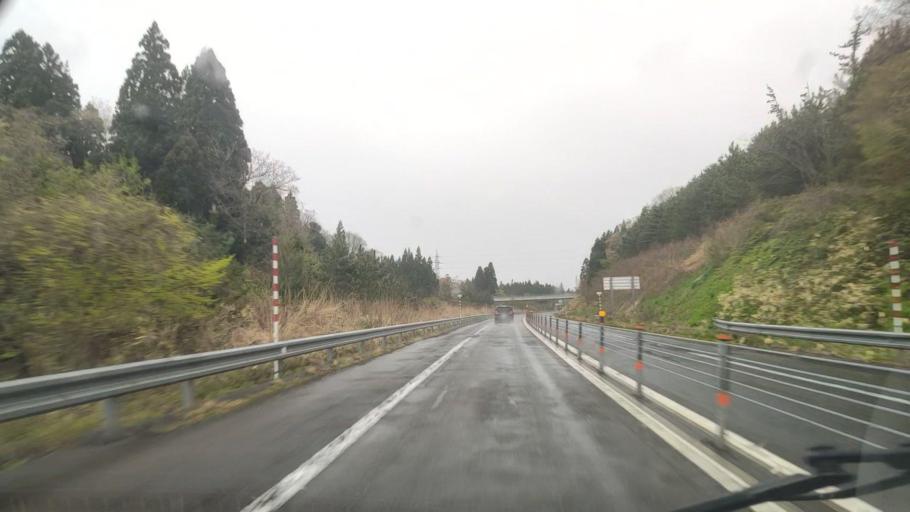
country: JP
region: Akita
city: Noshiromachi
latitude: 40.1697
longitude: 140.0520
